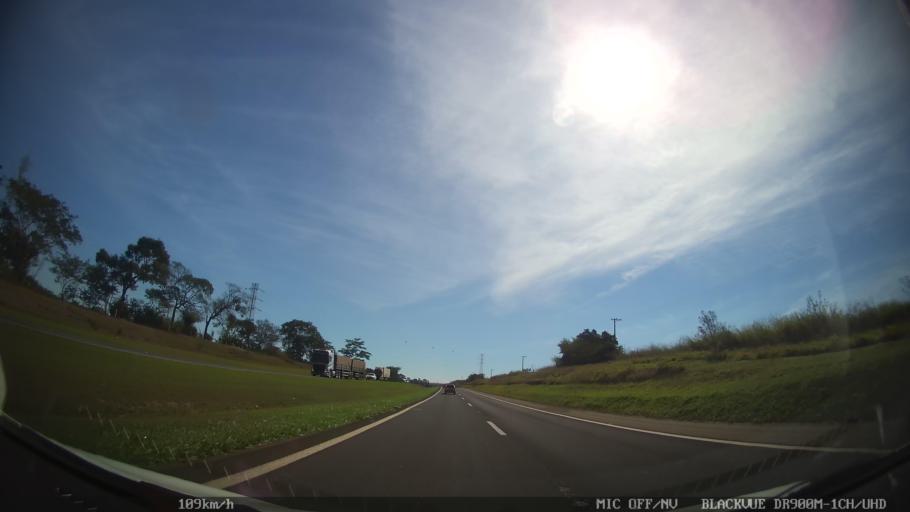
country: BR
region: Sao Paulo
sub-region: Porto Ferreira
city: Porto Ferreira
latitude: -21.8212
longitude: -47.4958
